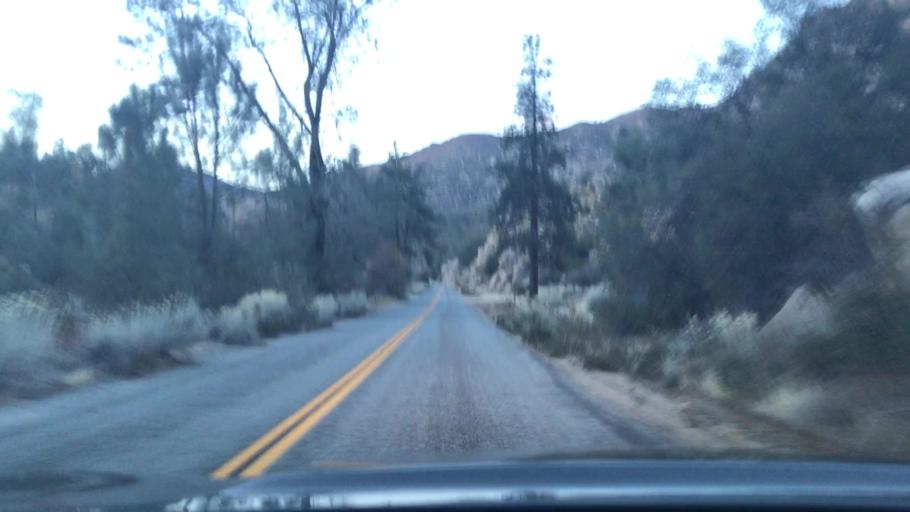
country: US
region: California
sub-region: Kern County
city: Kernville
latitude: 35.8967
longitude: -118.4668
